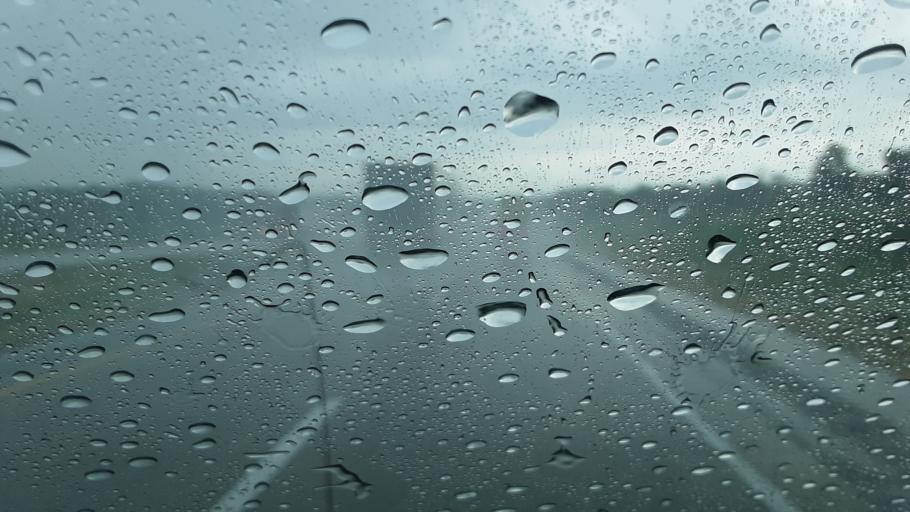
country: US
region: Iowa
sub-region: Pottawattamie County
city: Council Bluffs
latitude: 41.2908
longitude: -95.7776
